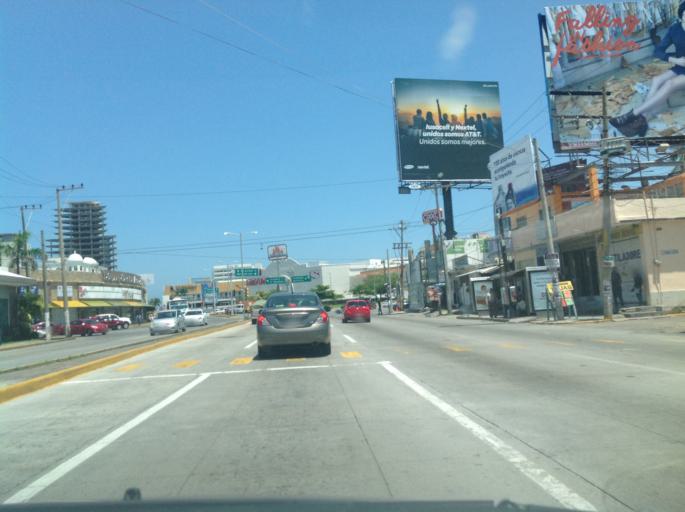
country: MX
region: Veracruz
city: Boca del Rio
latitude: 19.1403
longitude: -96.1097
